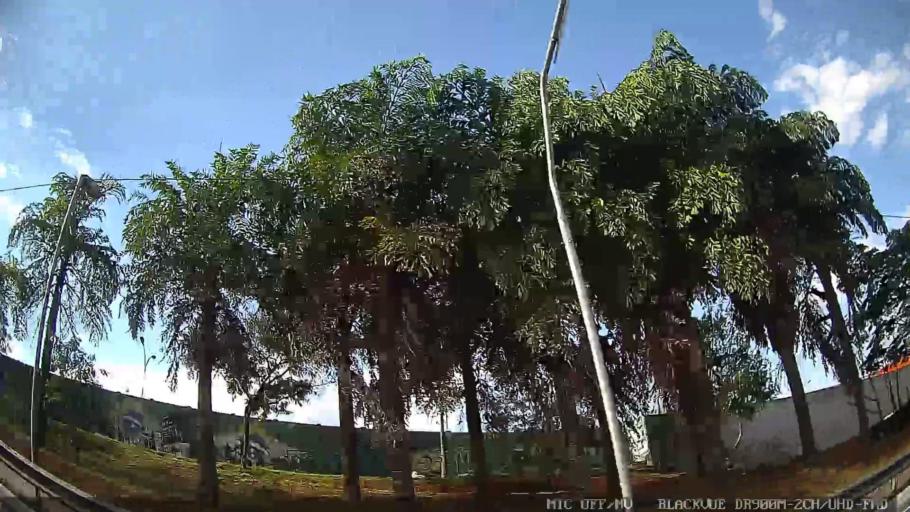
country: BR
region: Sao Paulo
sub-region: Guarulhos
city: Guarulhos
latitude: -23.5431
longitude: -46.4729
